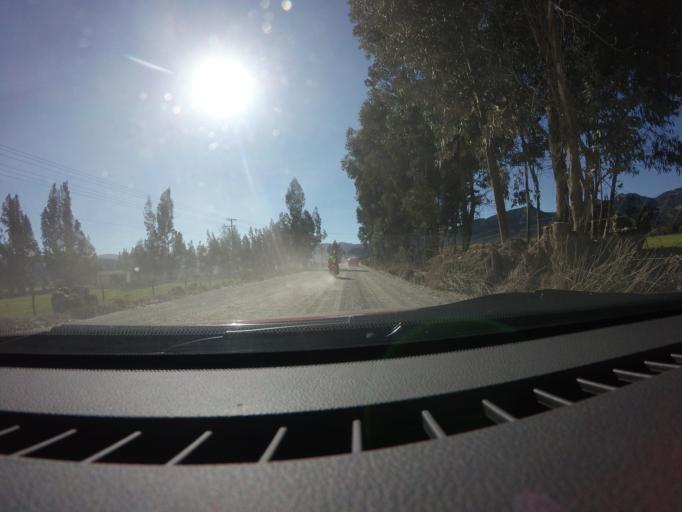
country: CO
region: Cundinamarca
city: Ubate
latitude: 5.2775
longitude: -73.8017
